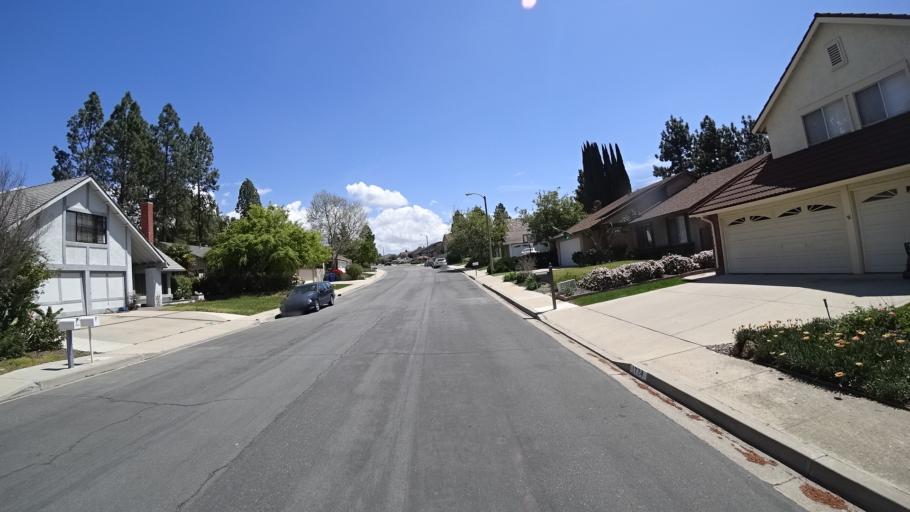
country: US
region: California
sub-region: Ventura County
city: Thousand Oaks
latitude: 34.2196
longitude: -118.8468
